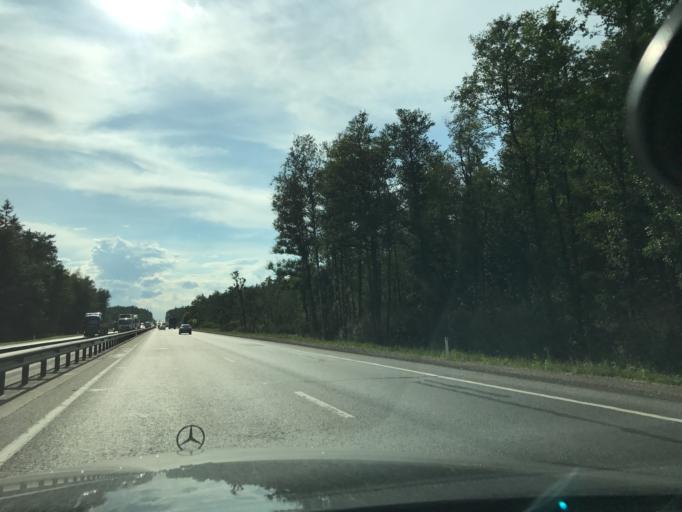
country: RU
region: Moskovskaya
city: Malaya Dubna
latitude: 55.8691
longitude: 38.9280
